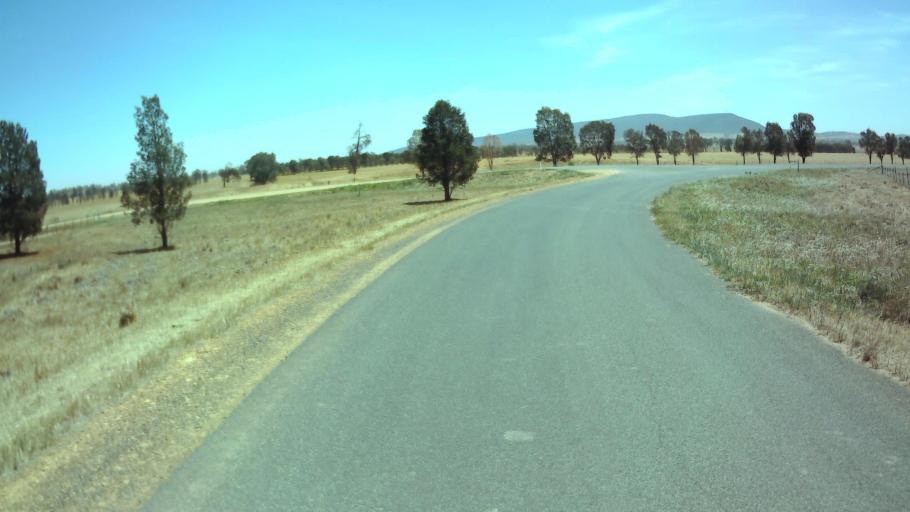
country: AU
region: New South Wales
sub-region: Weddin
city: Grenfell
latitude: -34.0492
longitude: 148.1744
